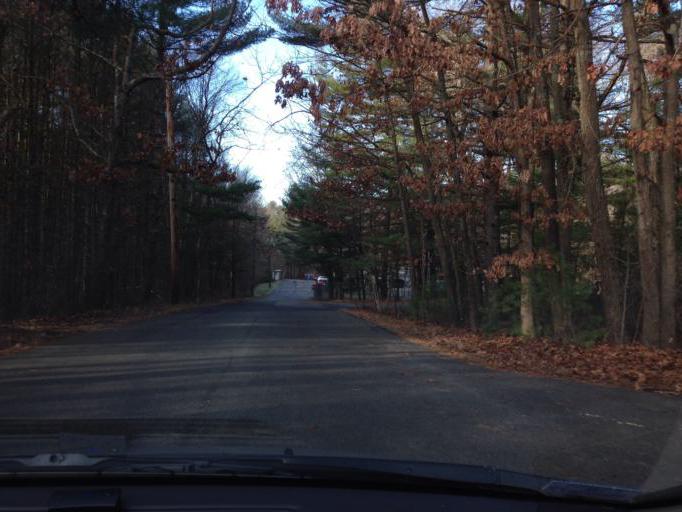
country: US
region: Massachusetts
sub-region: Middlesex County
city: Bedford
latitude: 42.5080
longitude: -71.2934
